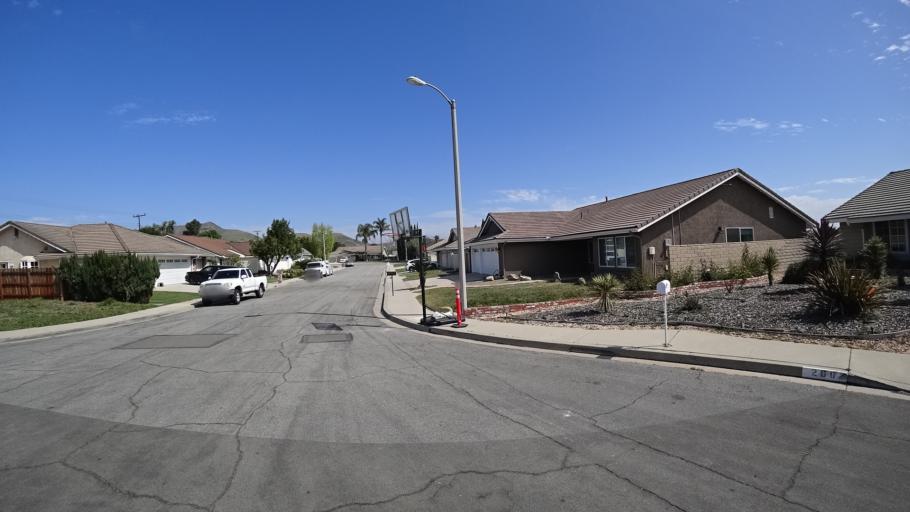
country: US
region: California
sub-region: Ventura County
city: Casa Conejo
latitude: 34.1822
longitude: -118.9380
